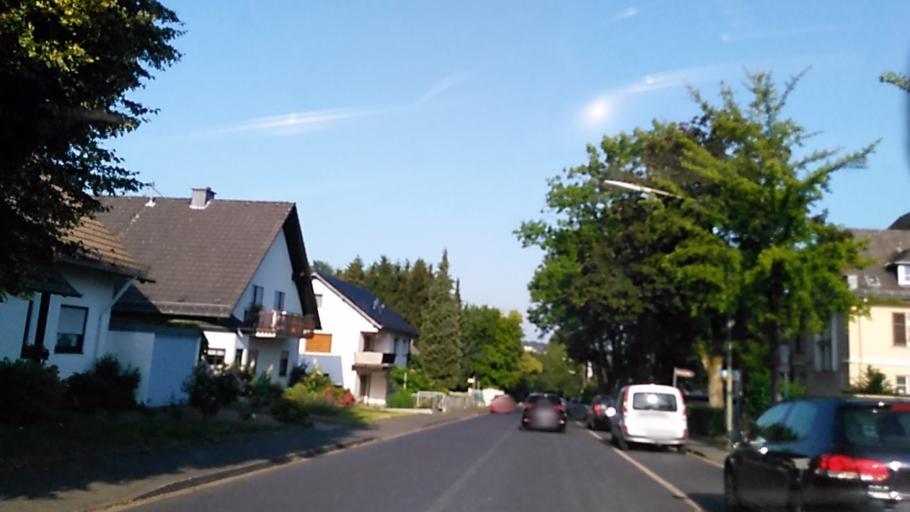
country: DE
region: North Rhine-Westphalia
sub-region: Regierungsbezirk Koln
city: Much
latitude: 50.9039
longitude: 7.4013
